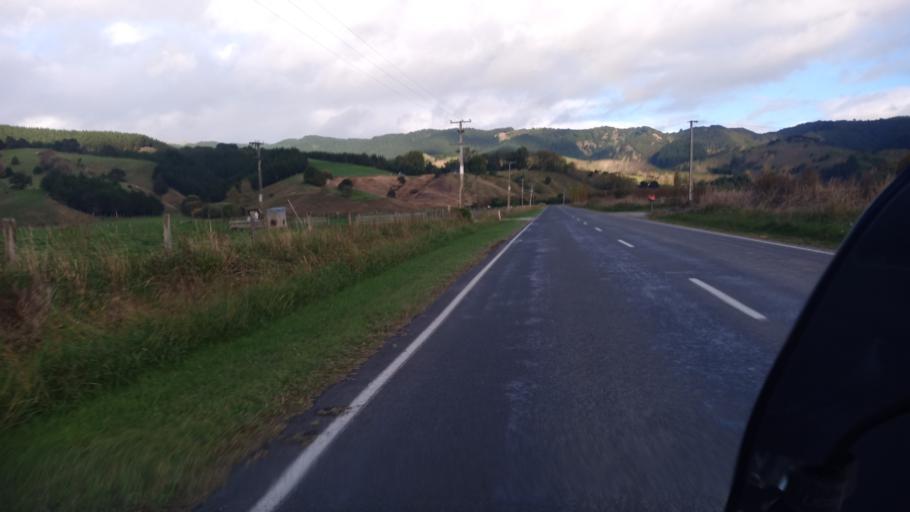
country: NZ
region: Gisborne
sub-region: Gisborne District
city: Gisborne
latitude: -38.6342
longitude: 177.8404
